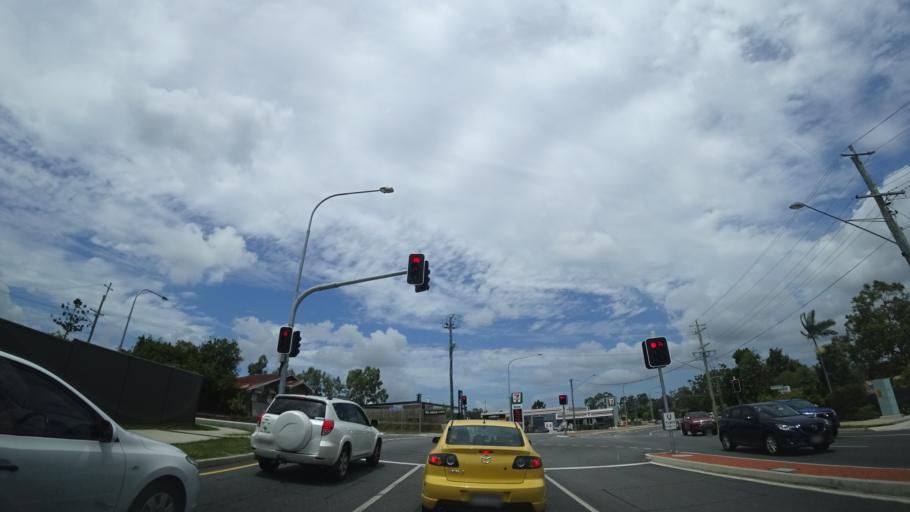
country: AU
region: Queensland
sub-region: Brisbane
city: Everton Park
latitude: -27.3910
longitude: 152.9711
